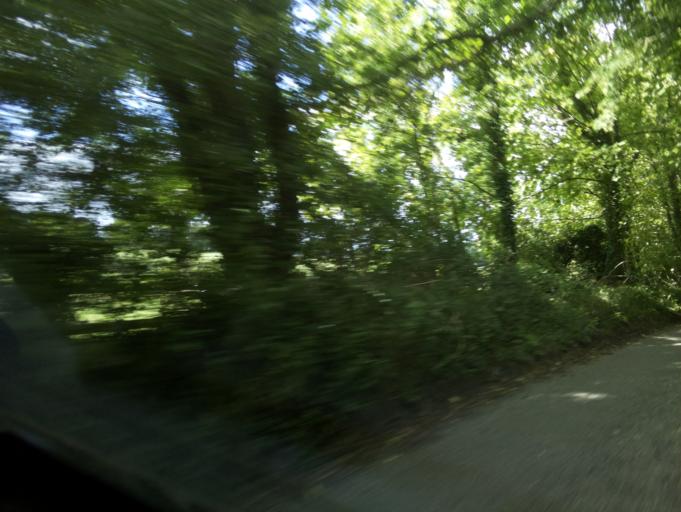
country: GB
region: England
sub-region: Hampshire
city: Winchester
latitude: 51.0823
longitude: -1.3748
